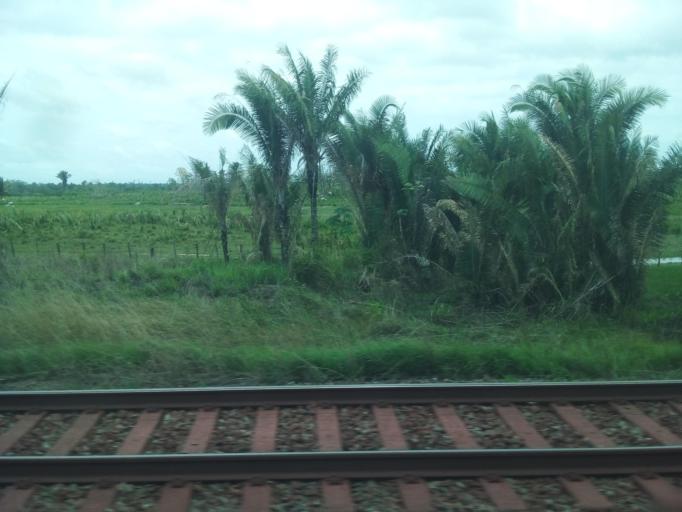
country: BR
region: Maranhao
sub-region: Santa Ines
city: Santa Ines
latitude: -3.6792
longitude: -45.3267
